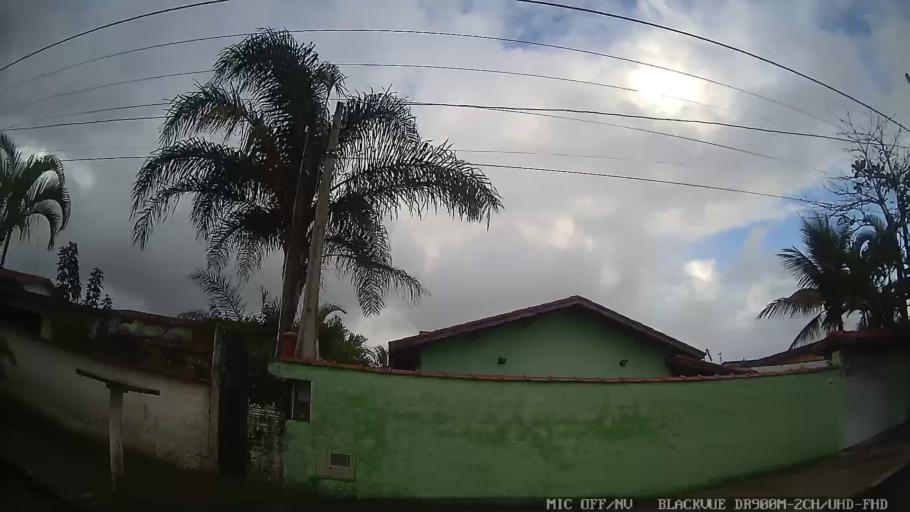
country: BR
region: Sao Paulo
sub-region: Itanhaem
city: Itanhaem
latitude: -24.2123
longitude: -46.8537
